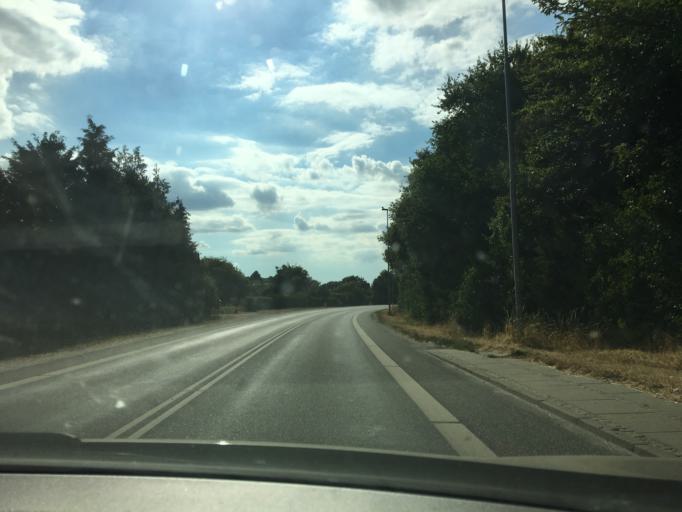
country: DK
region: South Denmark
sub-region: Nordfyns Kommune
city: Sonderso
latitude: 55.4198
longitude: 10.2660
